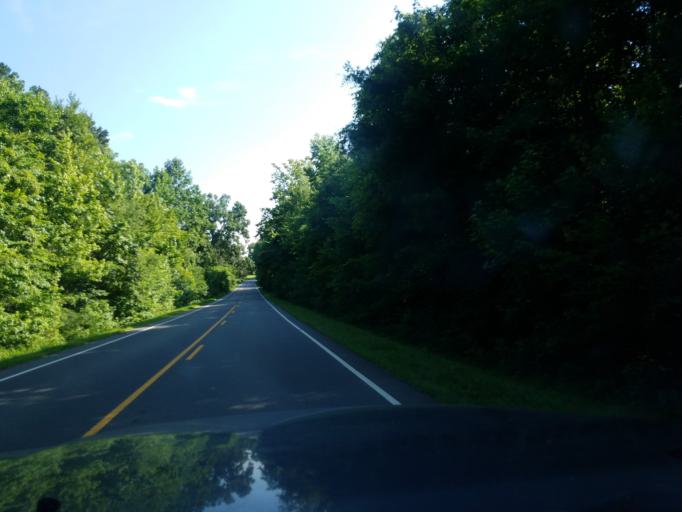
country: US
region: North Carolina
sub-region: Granville County
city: Creedmoor
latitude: 36.2384
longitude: -78.6965
